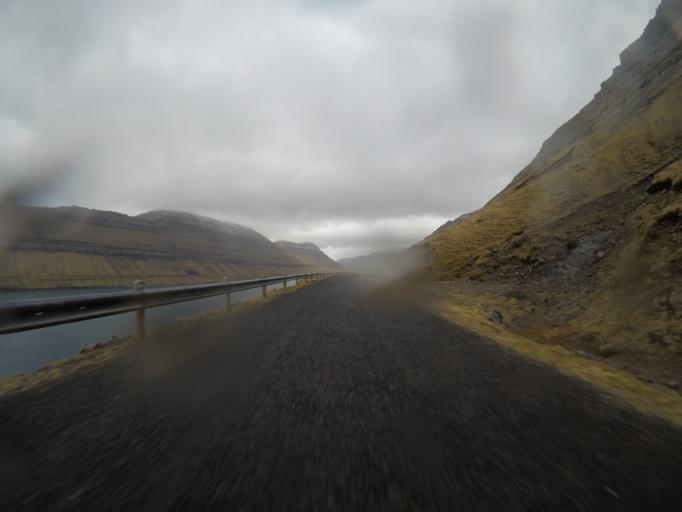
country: FO
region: Nordoyar
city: Klaksvik
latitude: 62.3296
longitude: -6.5705
